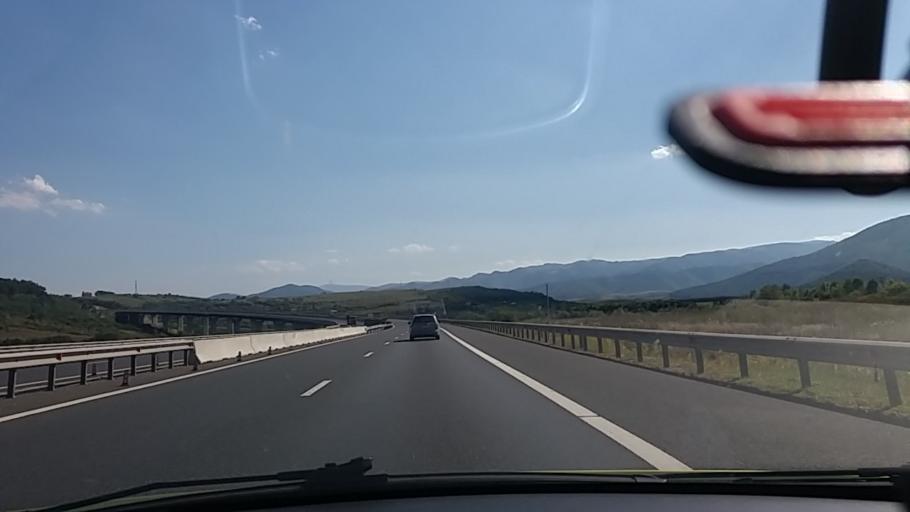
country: RO
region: Sibiu
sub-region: Comuna Orlat
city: Orlat
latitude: 45.7854
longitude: 23.9474
